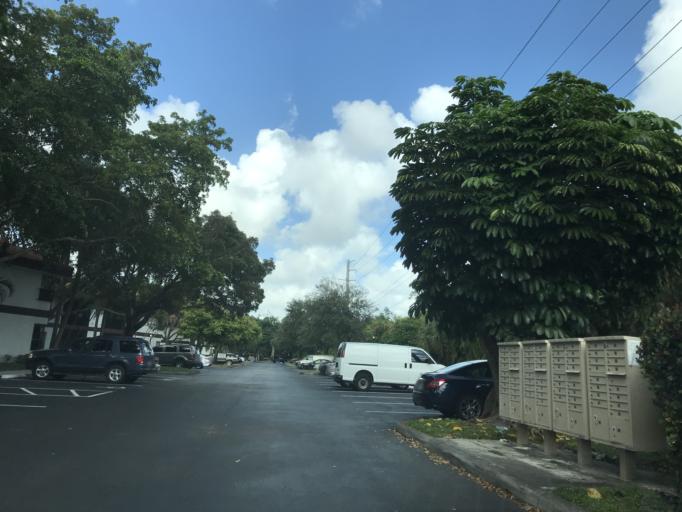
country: US
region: Florida
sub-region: Broward County
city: Coconut Creek
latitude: 26.2698
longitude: -80.1867
